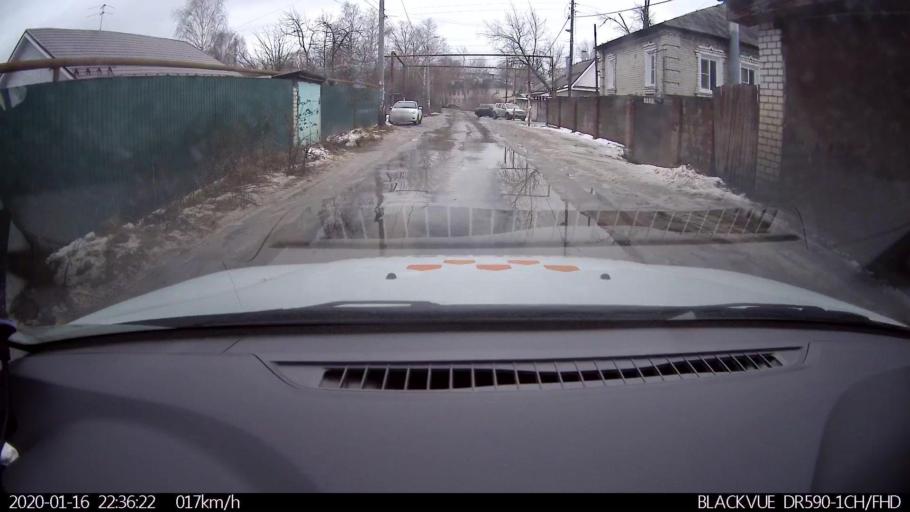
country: RU
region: Nizjnij Novgorod
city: Nizhniy Novgorod
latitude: 56.2784
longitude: 43.9075
